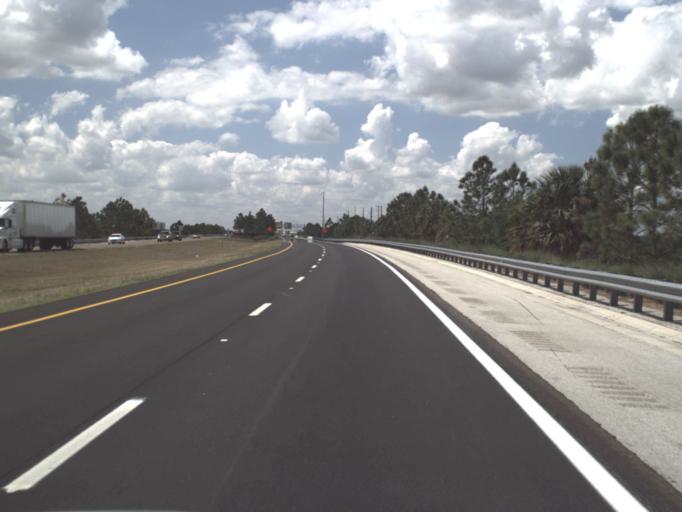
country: US
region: Florida
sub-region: Orange County
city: Oakland
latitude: 28.5101
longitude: -81.6079
